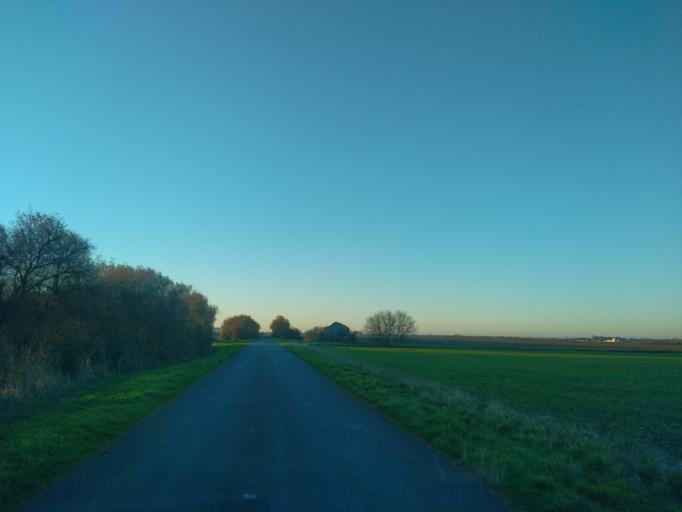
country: FR
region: Pays de la Loire
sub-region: Departement de la Vendee
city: Triaize
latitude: 46.3755
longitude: -1.2910
